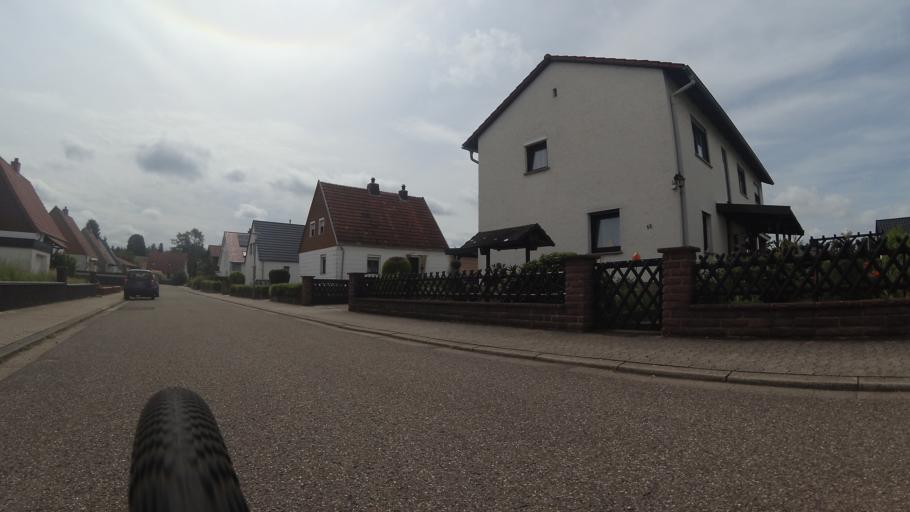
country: DE
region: Saarland
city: Spiesen-Elversberg
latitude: 49.2858
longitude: 7.1695
